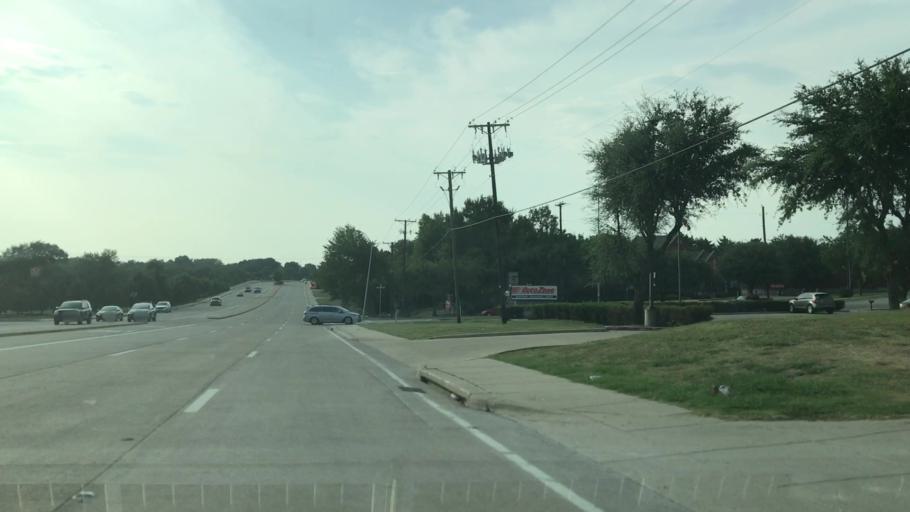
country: US
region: Texas
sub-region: Rockwall County
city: Rockwall
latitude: 32.9149
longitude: -96.4543
